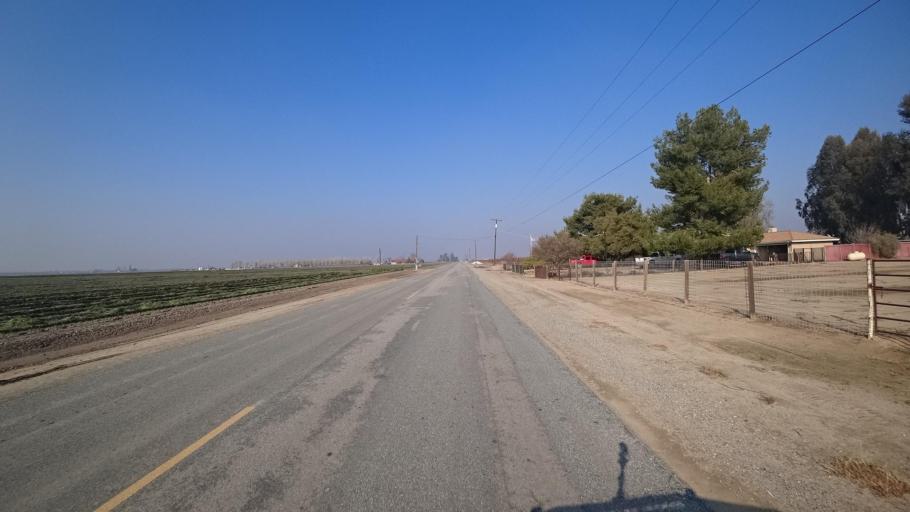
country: US
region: California
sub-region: Kern County
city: Greenfield
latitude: 35.2116
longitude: -119.0392
